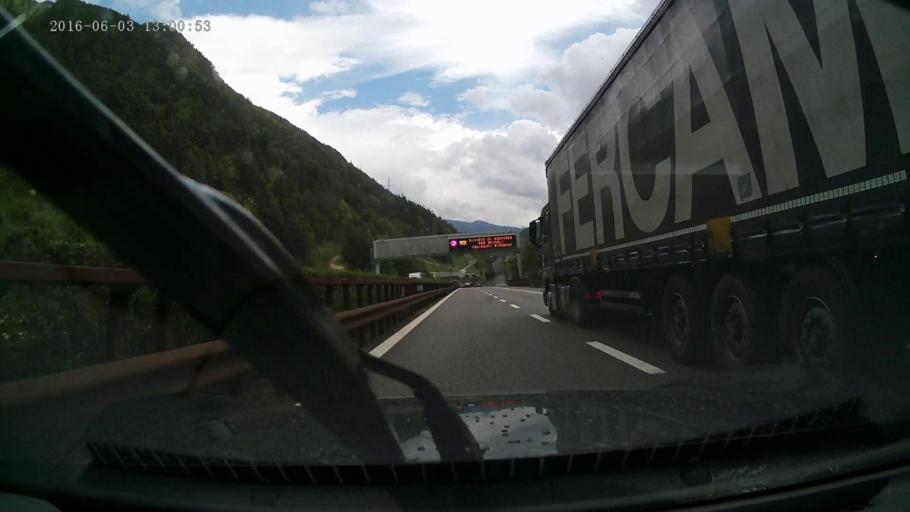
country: IT
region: Trentino-Alto Adige
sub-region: Bolzano
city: Fortezza
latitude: 46.7946
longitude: 11.6078
